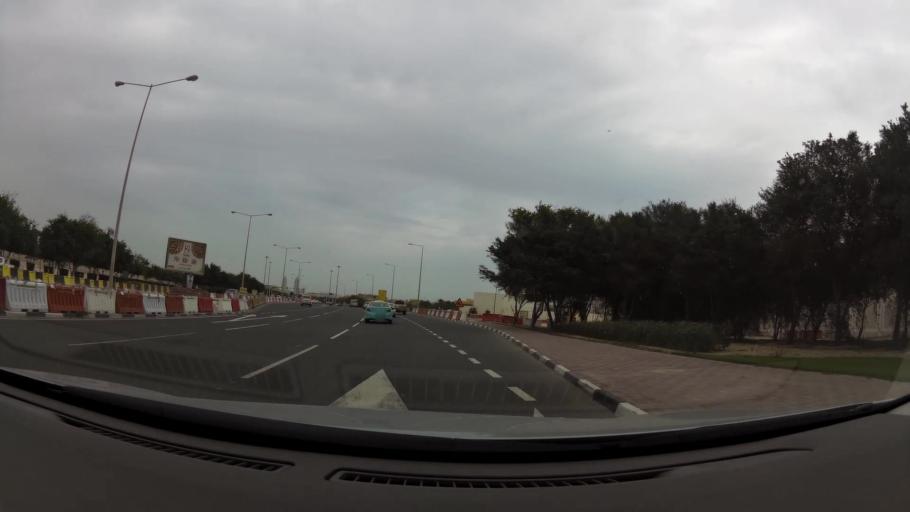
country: QA
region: Baladiyat ad Dawhah
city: Doha
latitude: 25.3488
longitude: 51.4985
